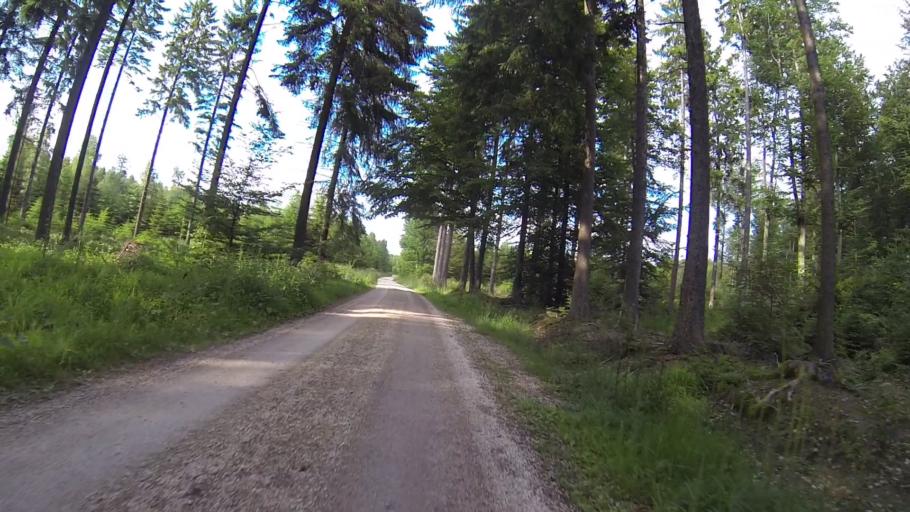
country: DE
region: Baden-Wuerttemberg
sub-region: Regierungsbezirk Stuttgart
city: Nattheim
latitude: 48.7151
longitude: 10.2712
